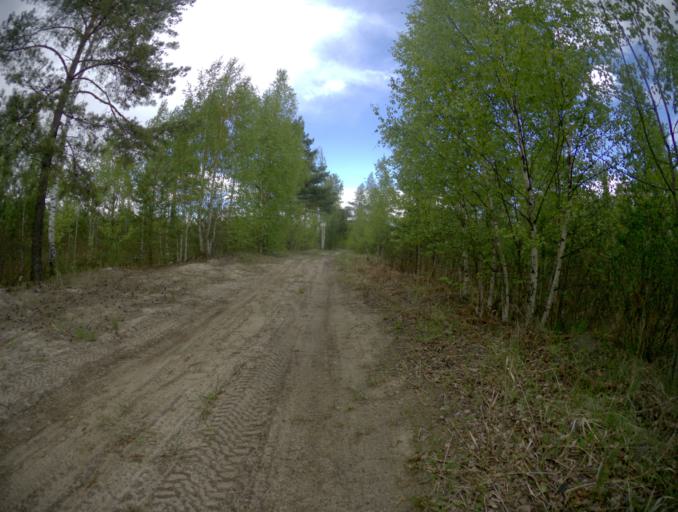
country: RU
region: Moskovskaya
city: Cherusti
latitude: 55.5802
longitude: 40.1020
